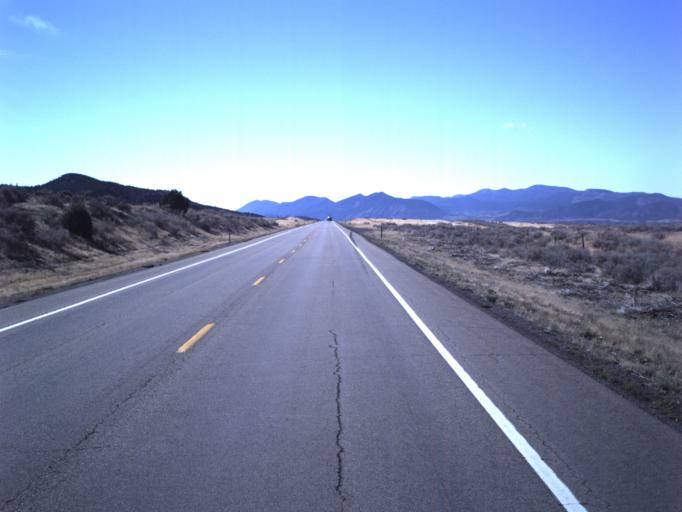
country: US
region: Utah
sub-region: Juab County
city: Nephi
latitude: 39.4340
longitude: -111.9173
